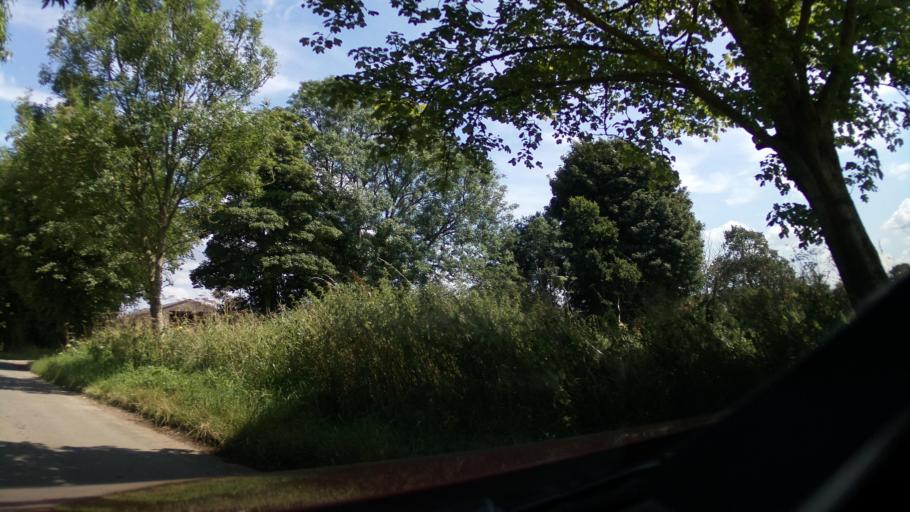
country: GB
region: England
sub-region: West Berkshire
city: Farnborough
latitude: 51.5106
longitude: -1.3949
